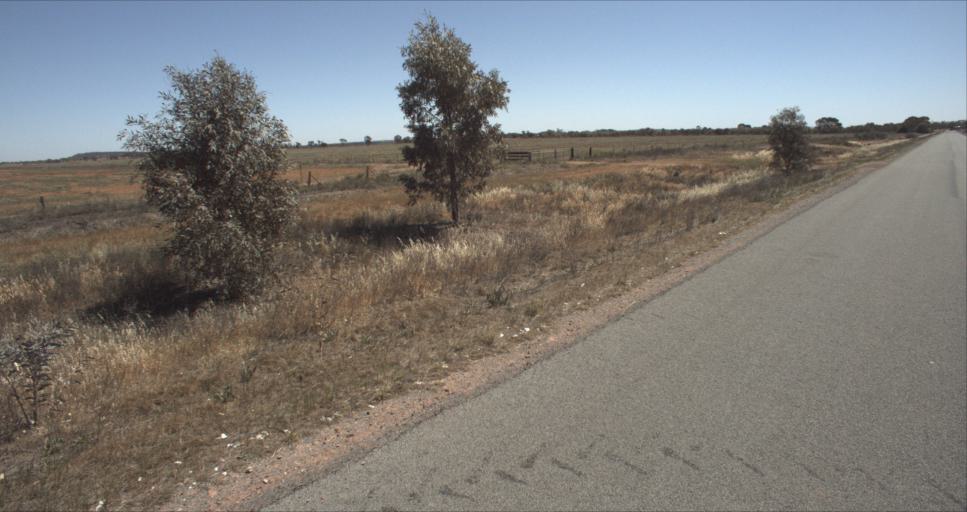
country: AU
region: New South Wales
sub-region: Leeton
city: Leeton
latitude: -34.4361
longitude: 146.2987
